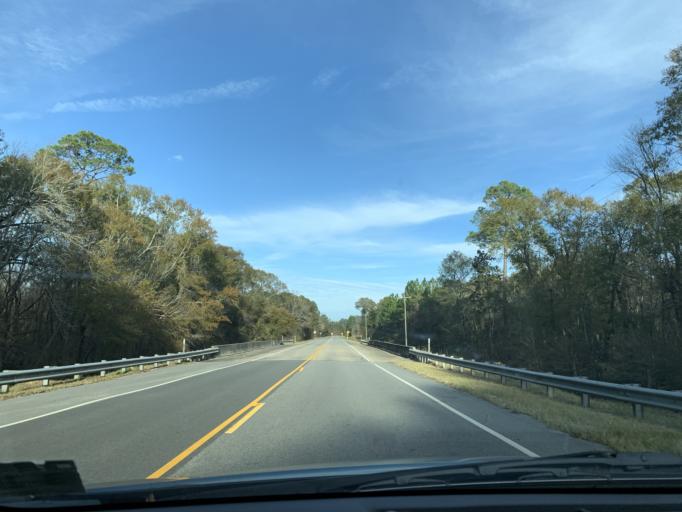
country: US
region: Georgia
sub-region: Tift County
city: Tifton
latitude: 31.6093
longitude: -83.4451
